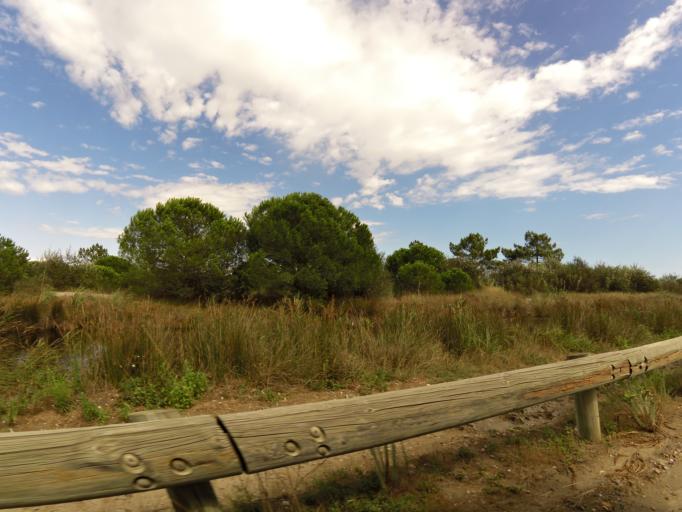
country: FR
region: Languedoc-Roussillon
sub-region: Departement du Gard
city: Le Grau-du-Roi
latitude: 43.4903
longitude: 4.1448
